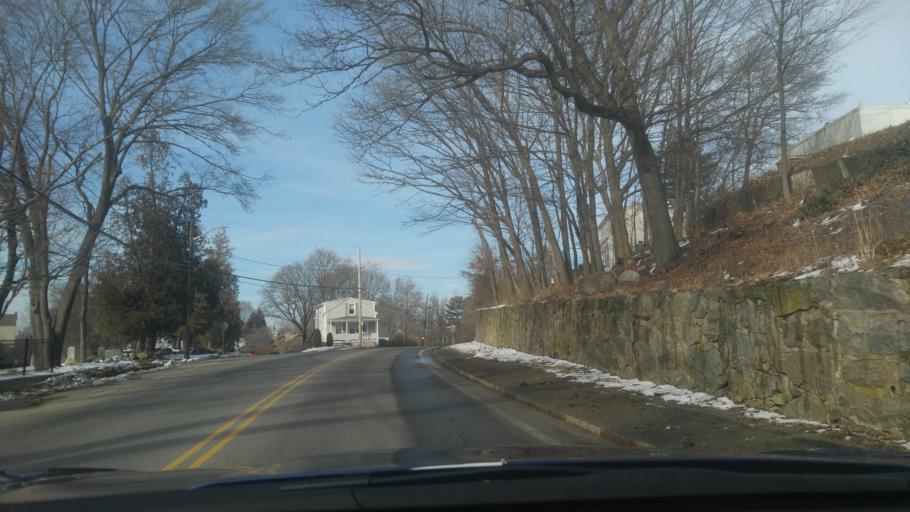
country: US
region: Rhode Island
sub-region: Kent County
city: West Warwick
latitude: 41.6928
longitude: -71.5206
